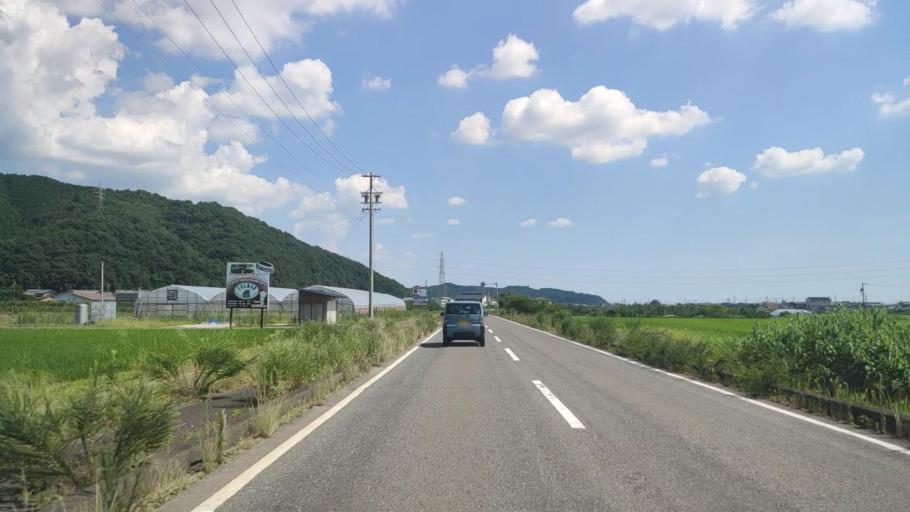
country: JP
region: Gifu
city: Godo
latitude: 35.4971
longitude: 136.6698
